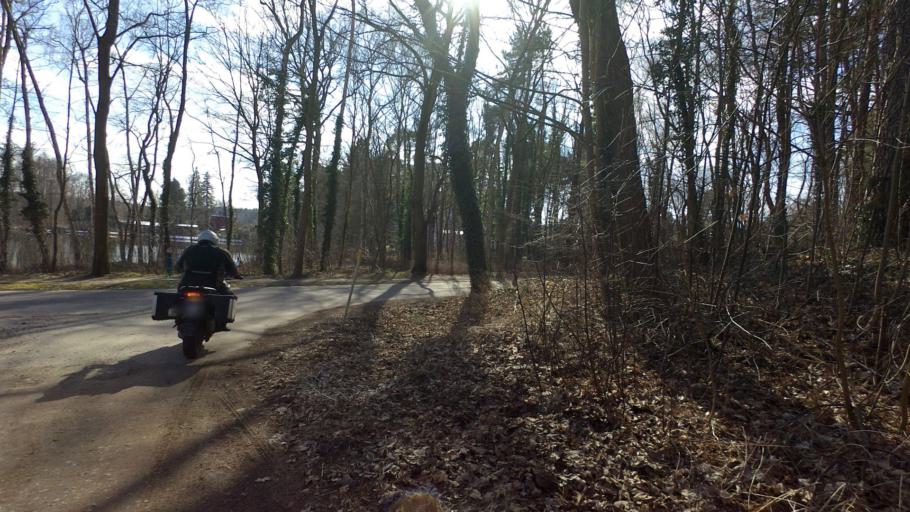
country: DE
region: Brandenburg
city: Biesenthal
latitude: 52.7685
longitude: 13.6133
